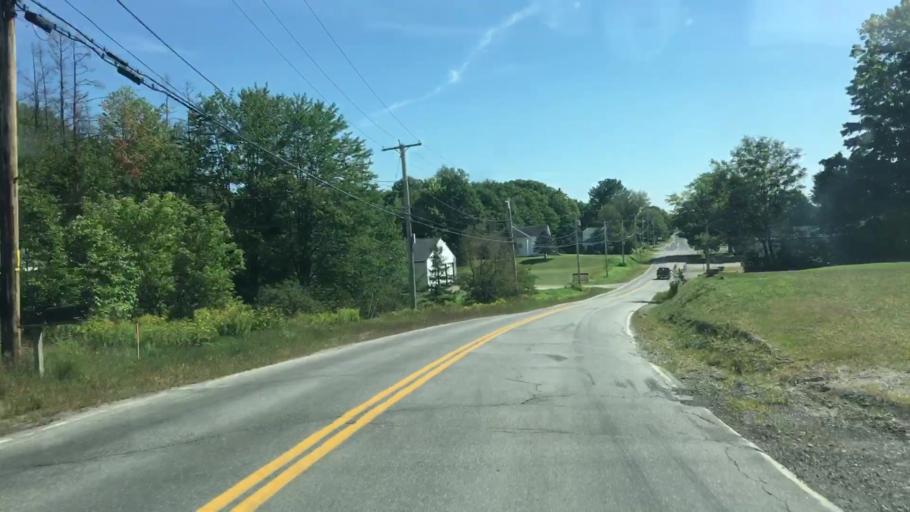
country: US
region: Maine
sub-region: Penobscot County
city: Bradford
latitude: 45.1692
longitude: -68.8471
